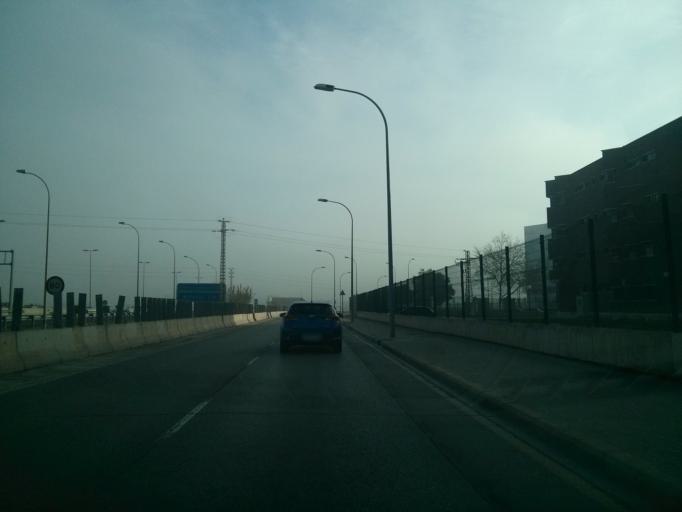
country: ES
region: Valencia
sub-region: Provincia de Valencia
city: Alboraya
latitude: 39.4842
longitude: -0.3467
